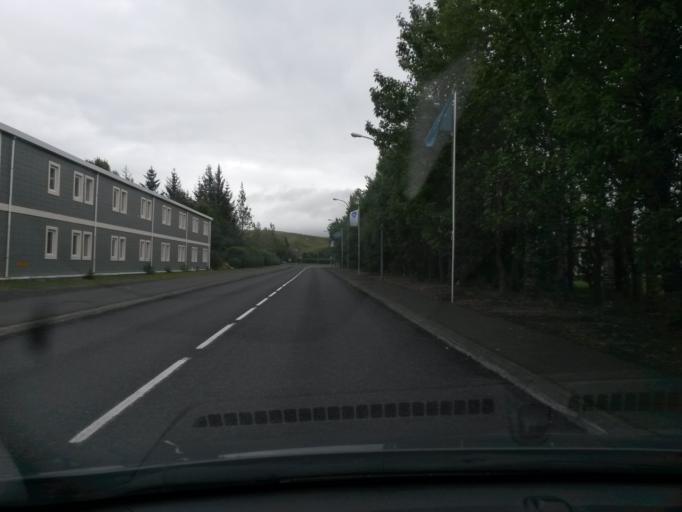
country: IS
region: South
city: Vestmannaeyjar
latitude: 63.7503
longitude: -20.2274
